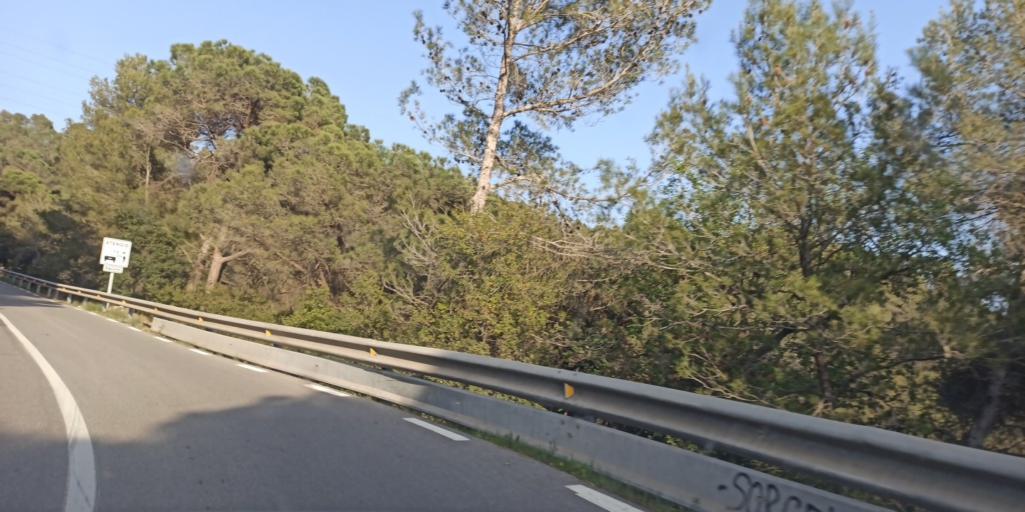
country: ES
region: Catalonia
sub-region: Provincia de Barcelona
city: Molins de Rei
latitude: 41.4279
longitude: 2.0436
